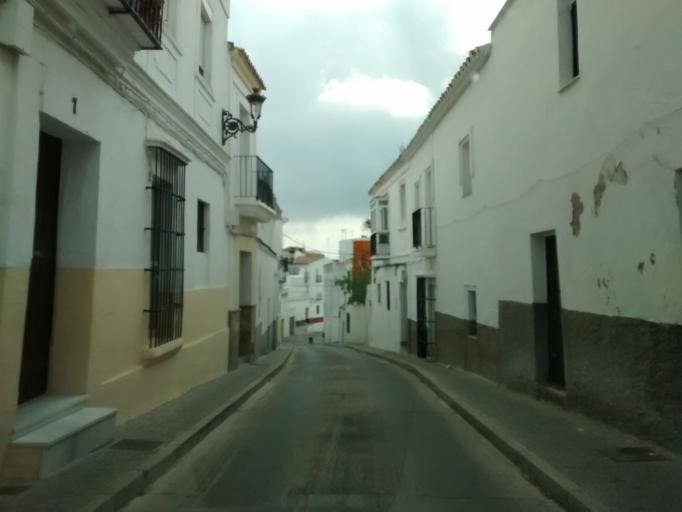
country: ES
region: Andalusia
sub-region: Provincia de Cadiz
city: Medina Sidonia
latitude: 36.4569
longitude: -5.9289
